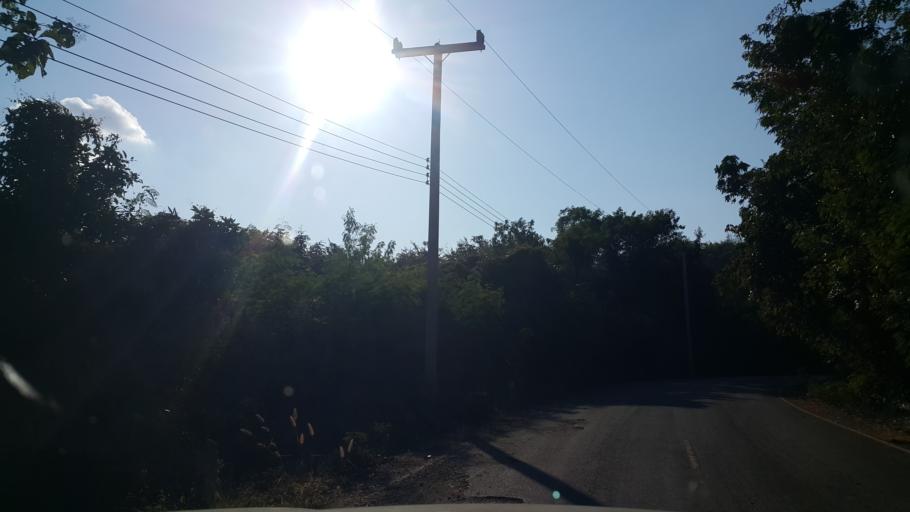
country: TH
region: Sukhothai
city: Thung Saliam
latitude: 17.3863
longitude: 99.5197
